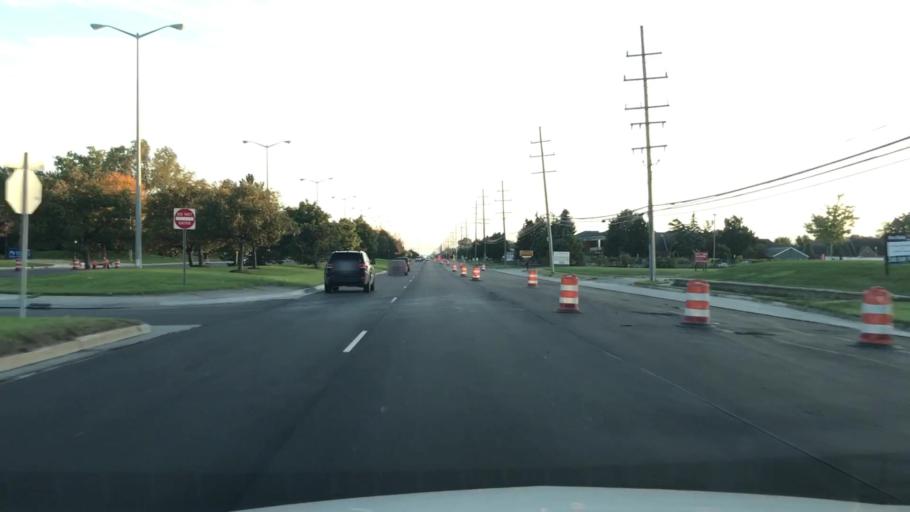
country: US
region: Michigan
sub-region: Macomb County
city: Sterling Heights
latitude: 42.5780
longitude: -83.0501
